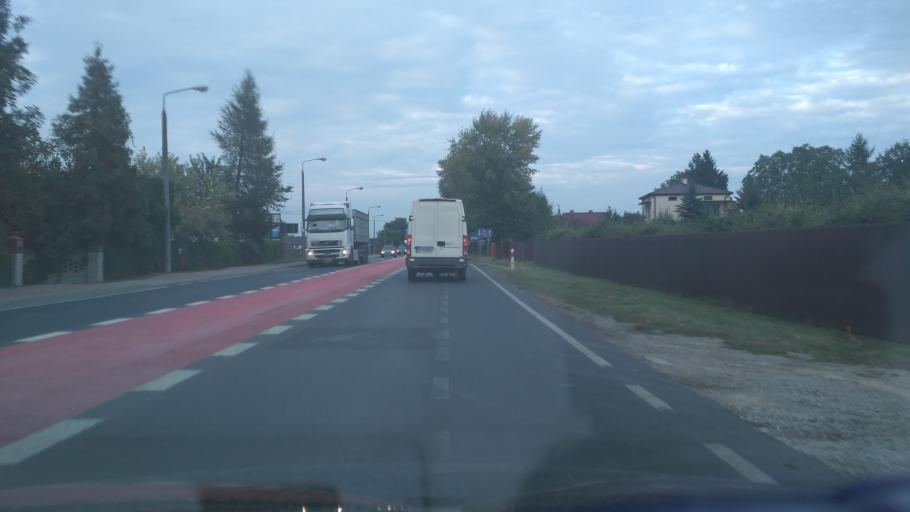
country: PL
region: Lublin Voivodeship
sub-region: Powiat lubelski
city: Jakubowice Murowane
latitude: 51.2688
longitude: 22.6379
